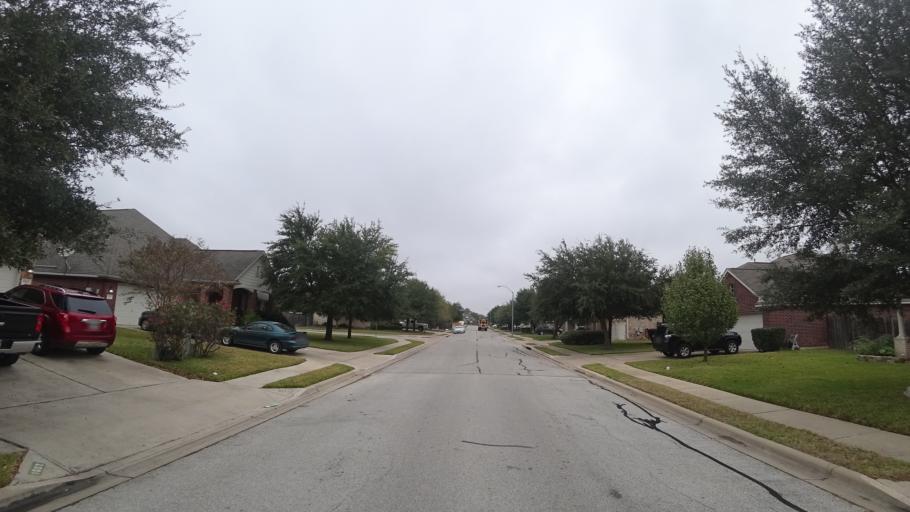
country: US
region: Texas
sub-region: Travis County
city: Pflugerville
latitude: 30.4275
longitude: -97.6171
